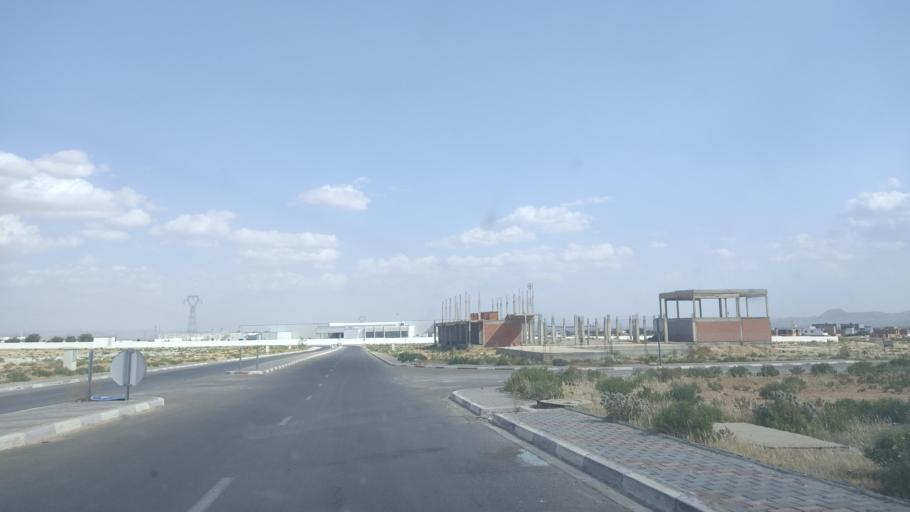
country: TN
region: Sidi Bu Zayd
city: Sidi Bouzid
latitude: 35.1070
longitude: 9.5441
